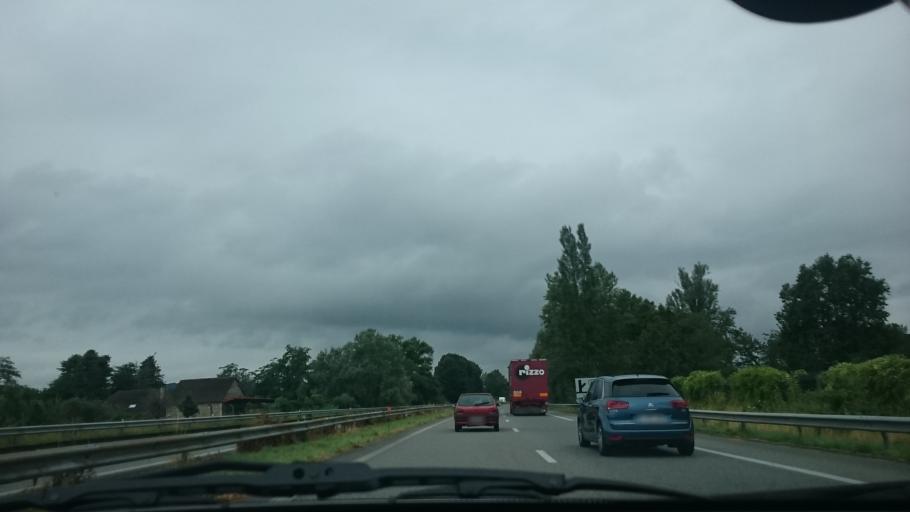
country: FR
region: Aquitaine
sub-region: Departement des Pyrenees-Atlantiques
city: Orthez
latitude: 43.4591
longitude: -0.7173
